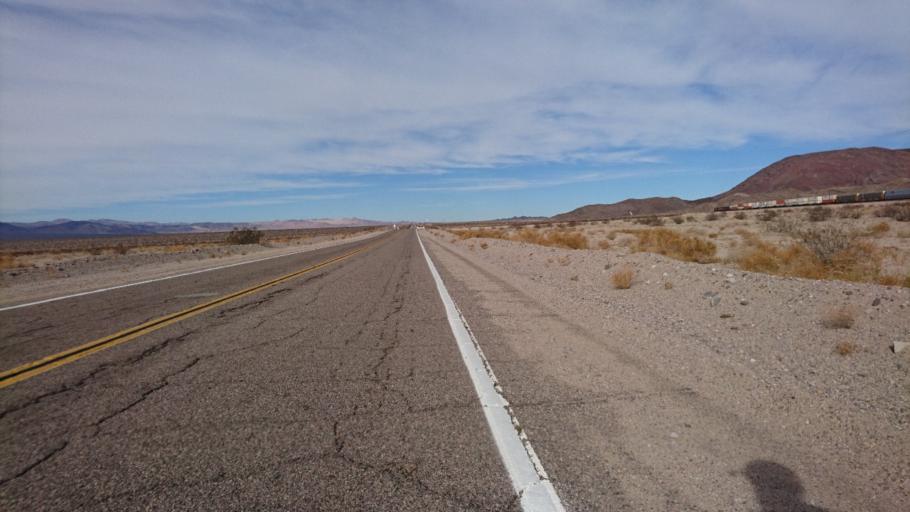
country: US
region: California
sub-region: San Bernardino County
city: Twentynine Palms
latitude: 34.5958
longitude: -115.9300
